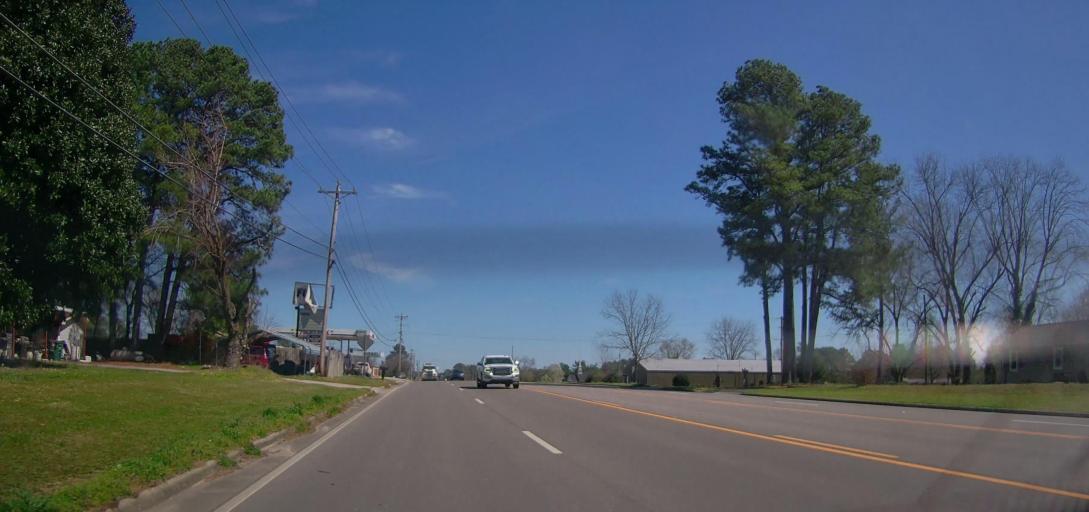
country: US
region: Alabama
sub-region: Cullman County
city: Cullman
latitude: 34.1790
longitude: -86.7456
